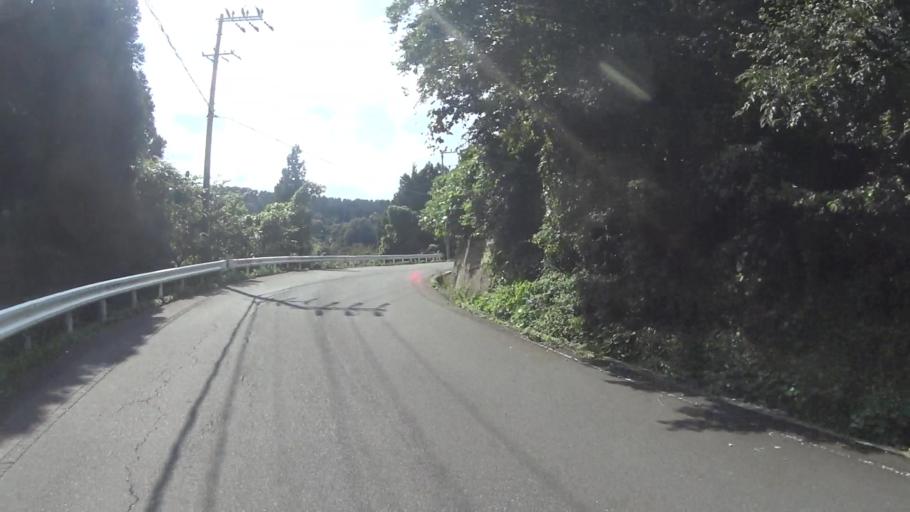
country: JP
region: Kyoto
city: Miyazu
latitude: 35.7098
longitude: 135.1934
